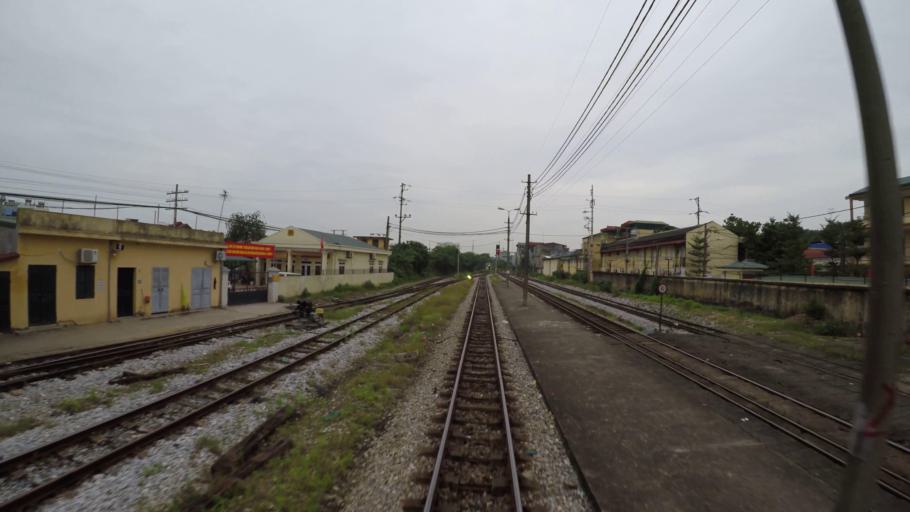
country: VN
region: Ha Noi
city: Trau Quy
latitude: 21.0249
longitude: 105.9276
